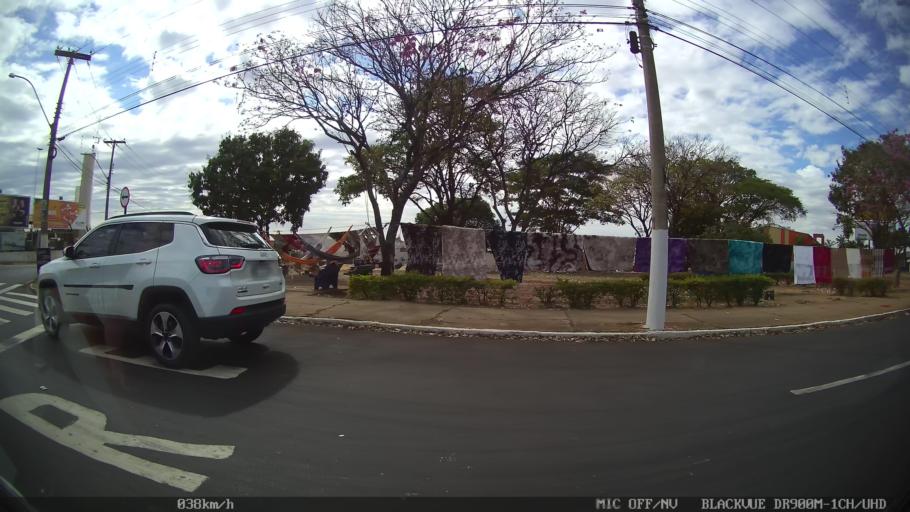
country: BR
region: Sao Paulo
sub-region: Bady Bassitt
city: Bady Bassitt
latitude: -20.8075
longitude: -49.5061
